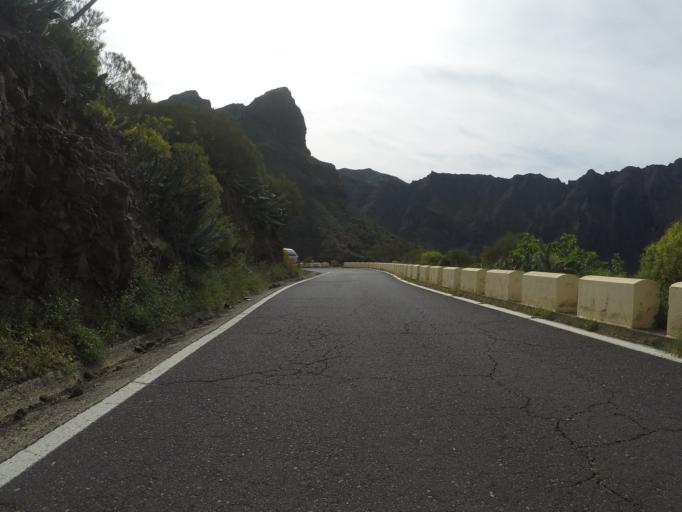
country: ES
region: Canary Islands
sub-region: Provincia de Santa Cruz de Tenerife
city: Santiago del Teide
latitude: 28.3107
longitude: -16.8447
